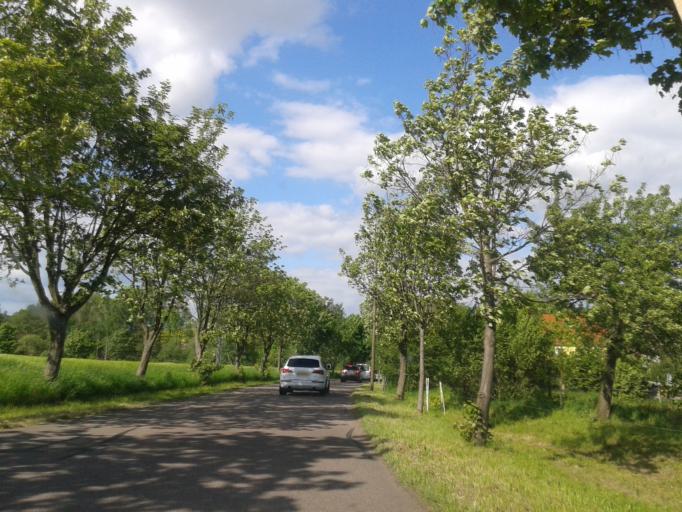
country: DE
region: Saxony
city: Wilsdruff
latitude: 51.0557
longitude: 13.4839
